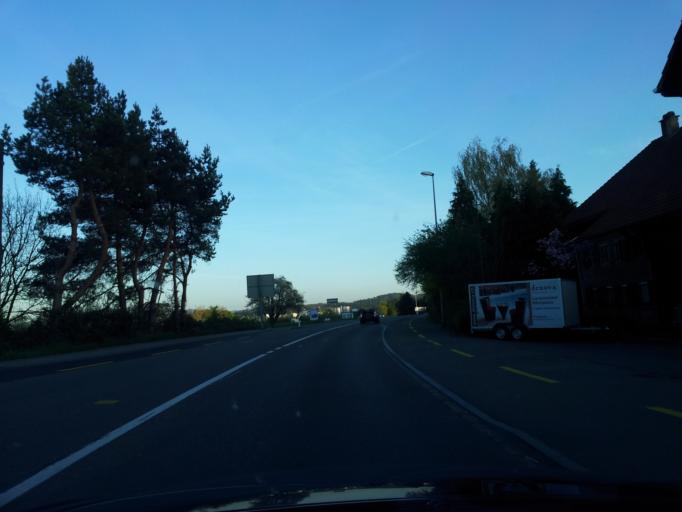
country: CH
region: Aargau
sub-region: Bezirk Baden
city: Spreitenbach
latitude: 47.4176
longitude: 8.3752
